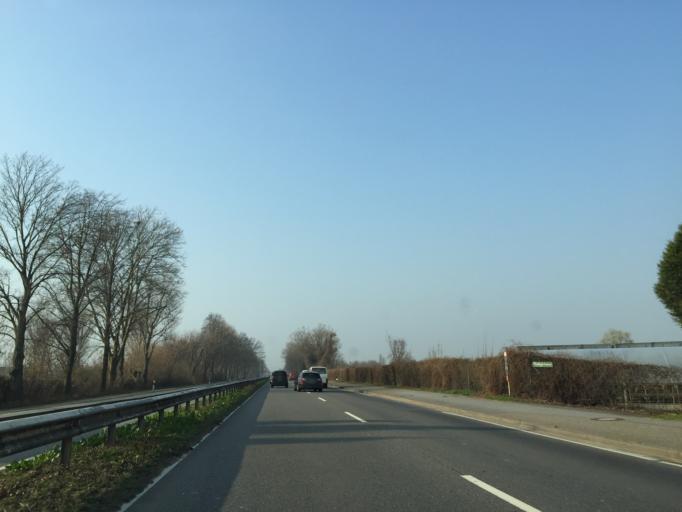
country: DE
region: Baden-Wuerttemberg
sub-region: Karlsruhe Region
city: Heidelberg
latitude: 49.3947
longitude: 8.6683
